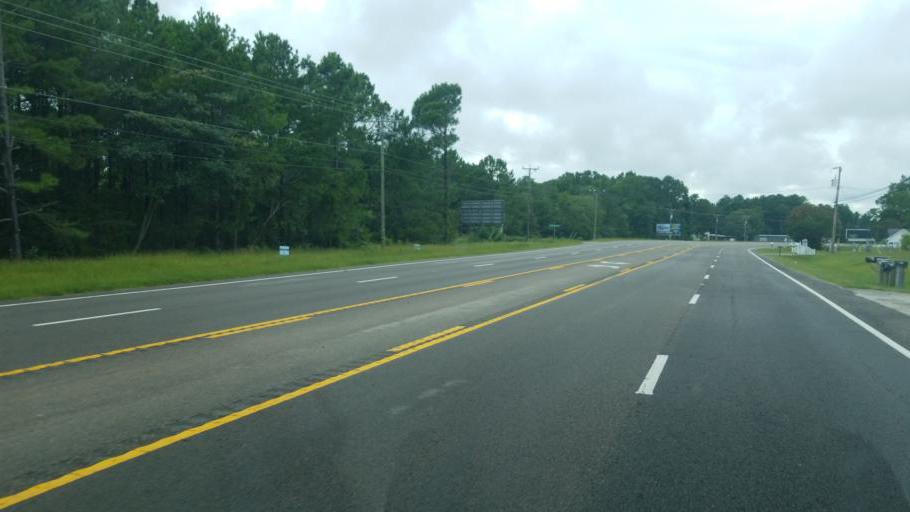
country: US
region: North Carolina
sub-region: Dare County
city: Southern Shores
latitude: 36.1791
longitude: -75.8637
